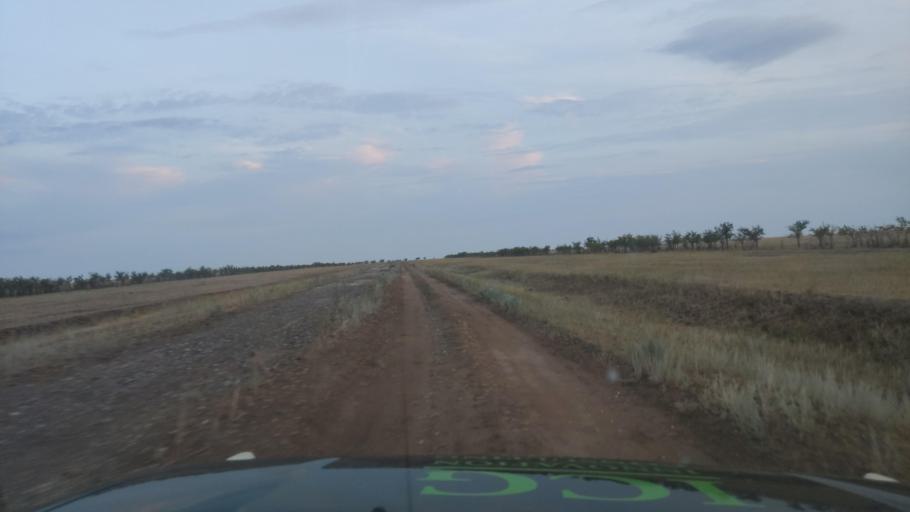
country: KZ
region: Pavlodar
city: Pavlodar
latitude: 52.1990
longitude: 77.6102
